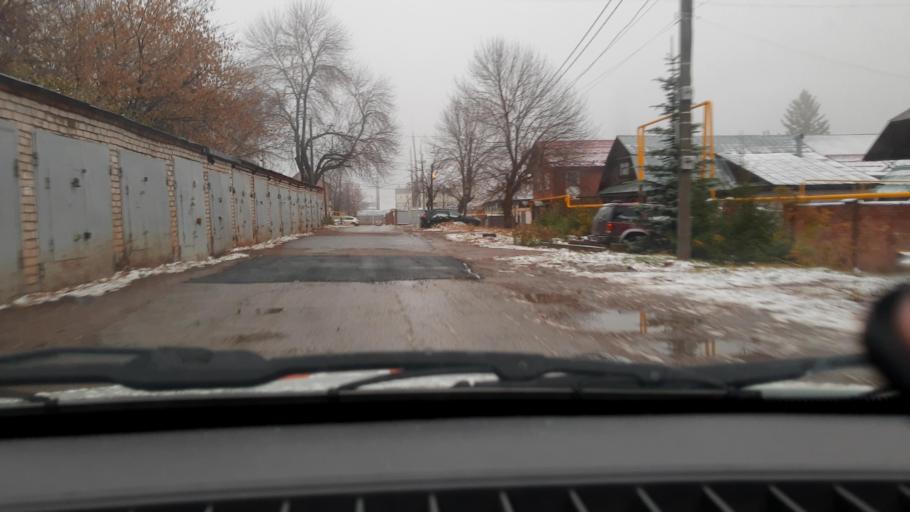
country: RU
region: Bashkortostan
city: Ufa
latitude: 54.7217
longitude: 55.9214
